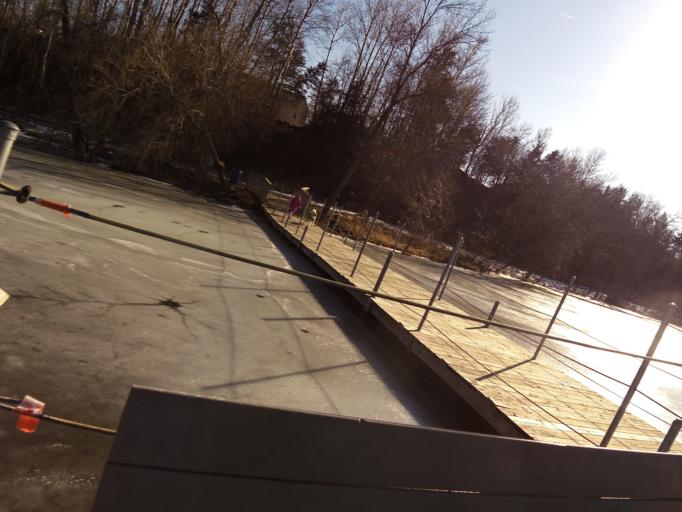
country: US
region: Minnesota
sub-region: Scott County
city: Prior Lake
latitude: 44.7006
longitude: -93.4405
